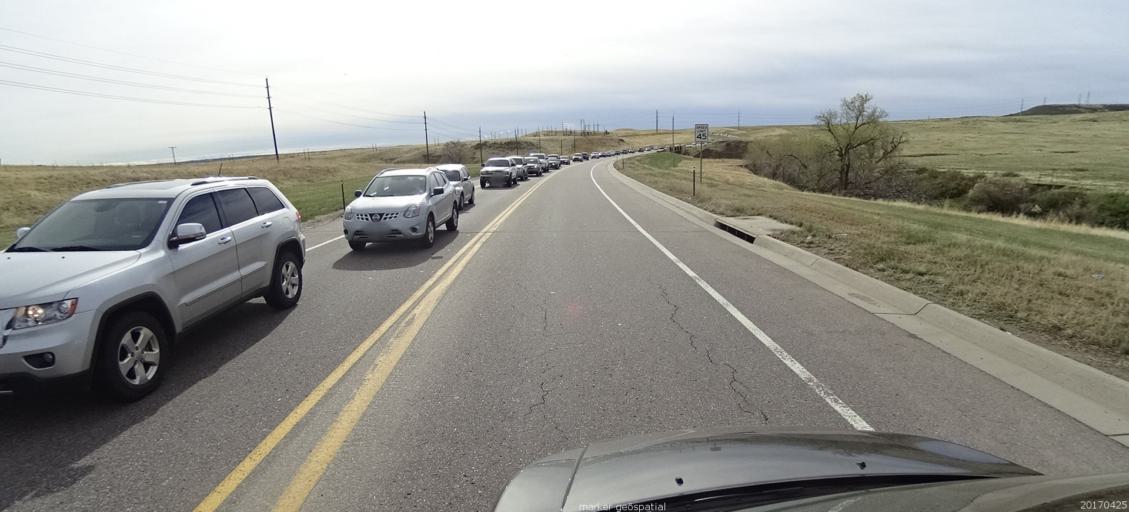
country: US
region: Colorado
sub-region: Douglas County
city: Meridian
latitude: 39.5231
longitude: -104.8559
